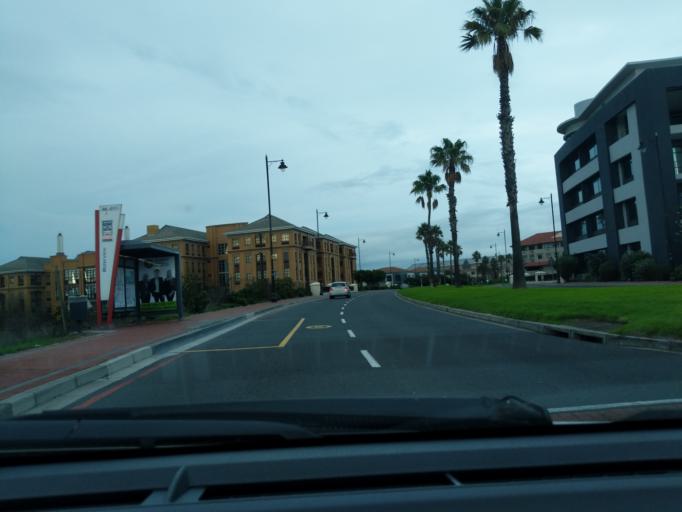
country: ZA
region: Western Cape
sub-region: City of Cape Town
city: Sunset Beach
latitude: -33.8867
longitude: 18.5203
